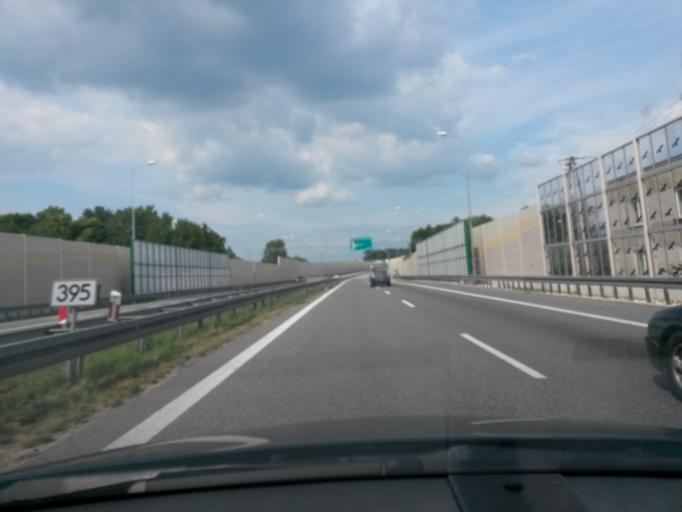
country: PL
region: Lodz Voivodeship
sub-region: Powiat skierniewicki
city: Kowiesy
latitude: 51.8385
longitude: 20.3465
